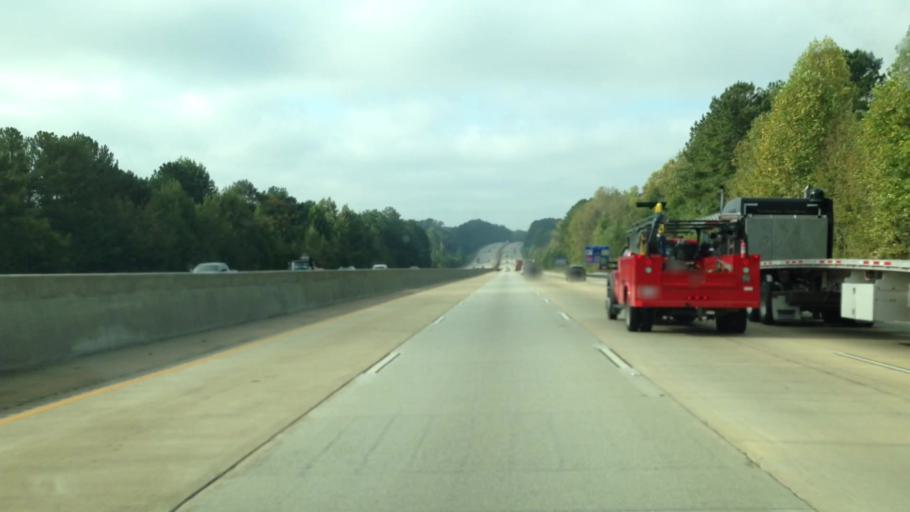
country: US
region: Georgia
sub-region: Coweta County
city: Newnan
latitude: 33.4176
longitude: -84.7310
